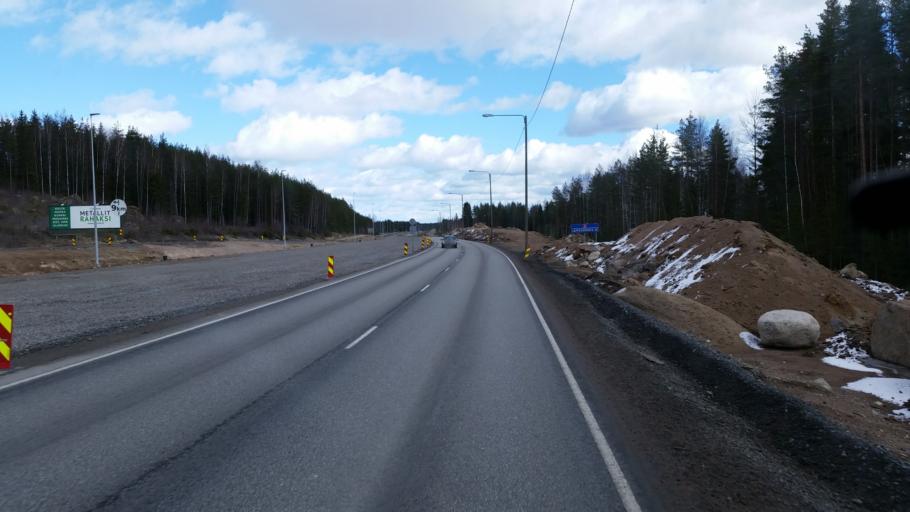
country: FI
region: South Karelia
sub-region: Lappeenranta
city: Luumaeki
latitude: 60.9294
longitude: 27.6379
